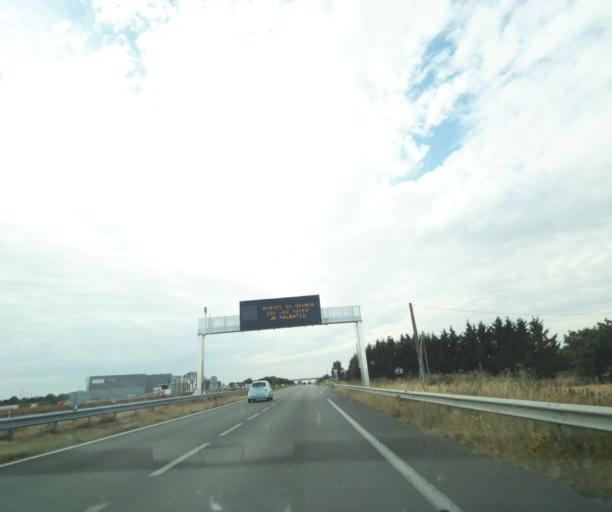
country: FR
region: Poitou-Charentes
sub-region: Departement de la Charente-Maritime
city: Angoulins
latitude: 46.1006
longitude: -1.0926
